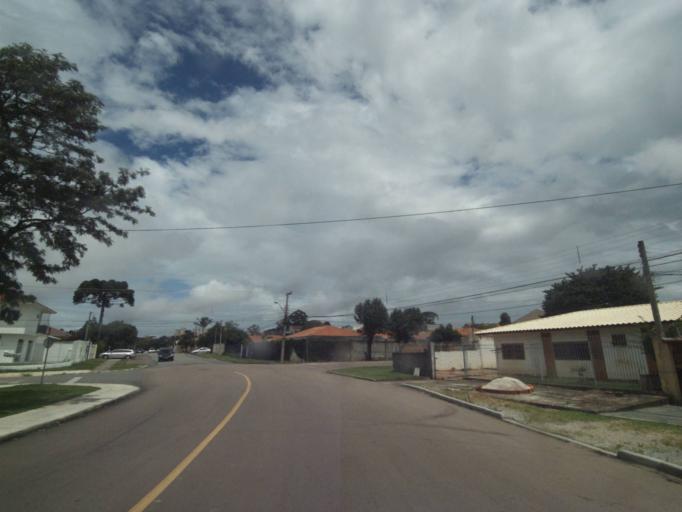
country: BR
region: Parana
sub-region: Curitiba
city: Curitiba
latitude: -25.4859
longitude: -49.2798
